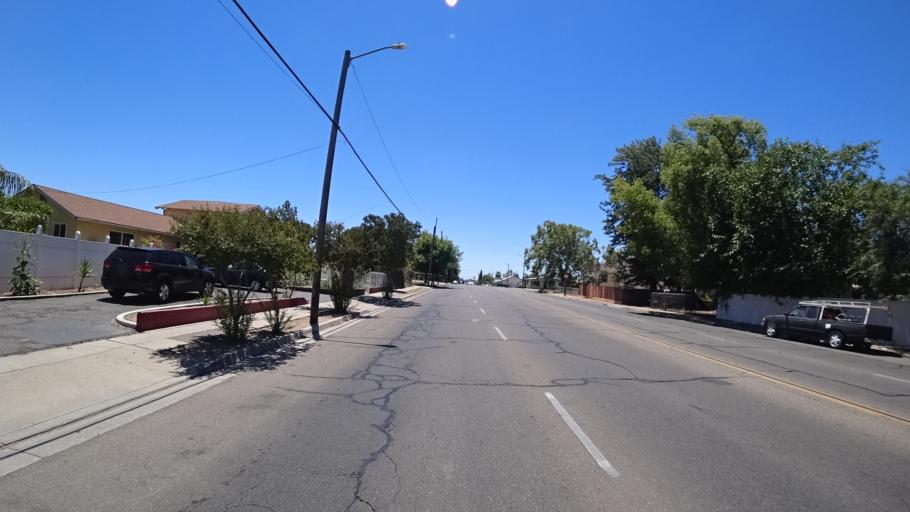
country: US
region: California
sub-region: Fresno County
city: Fresno
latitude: 36.7401
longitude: -119.7454
